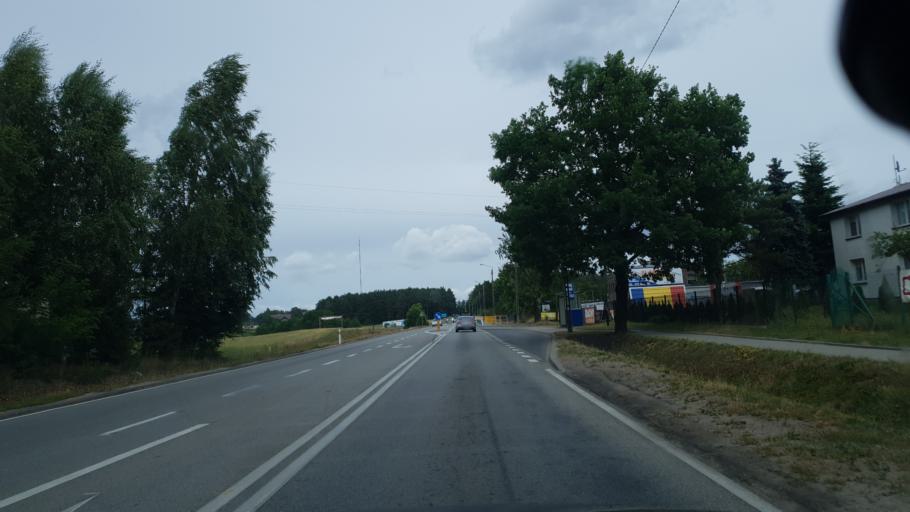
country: PL
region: Pomeranian Voivodeship
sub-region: Powiat kartuski
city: Chwaszczyno
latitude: 54.4358
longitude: 18.4046
